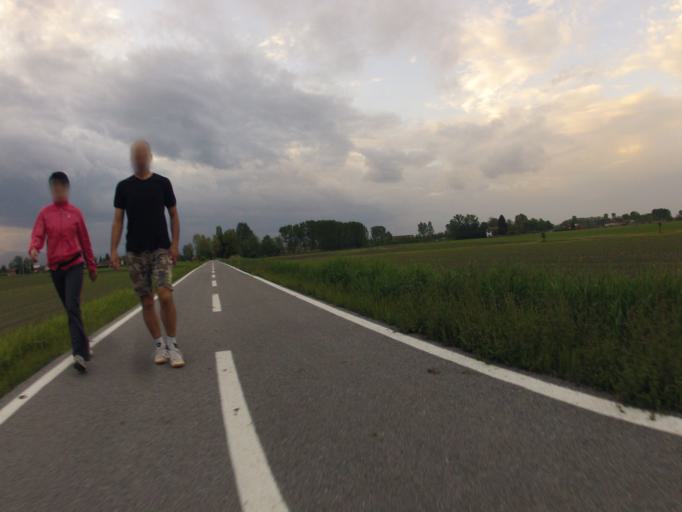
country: IT
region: Piedmont
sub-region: Provincia di Torino
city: Vigone
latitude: 44.8288
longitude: 7.4939
